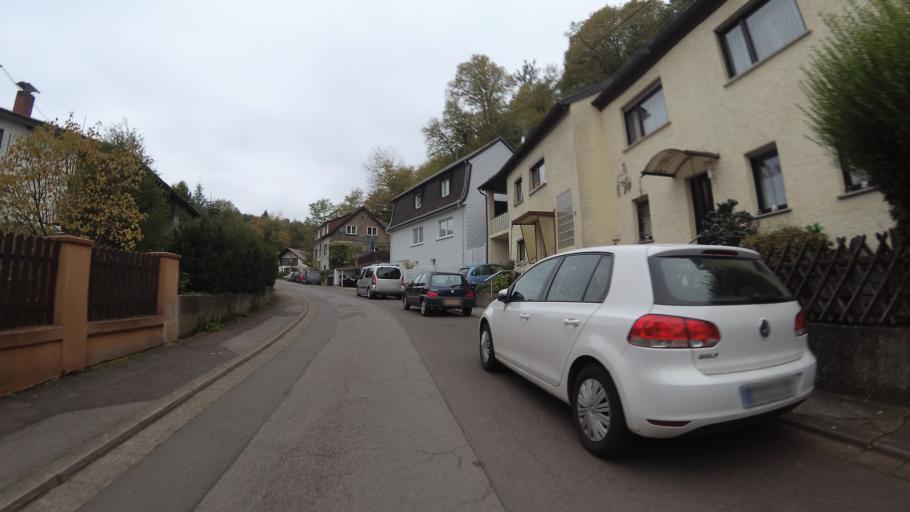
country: DE
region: Saarland
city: Blieskastel
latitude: 49.2666
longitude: 7.2787
